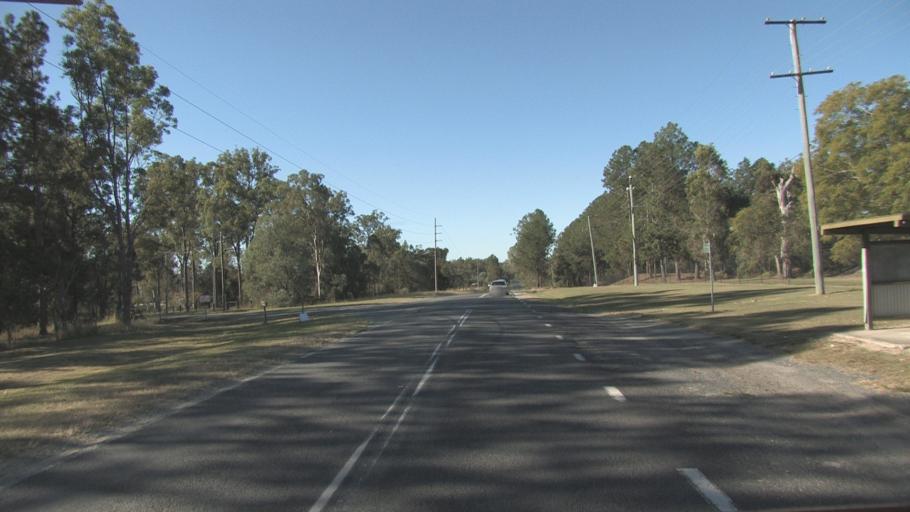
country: AU
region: Queensland
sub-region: Logan
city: North Maclean
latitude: -27.7878
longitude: 153.0450
